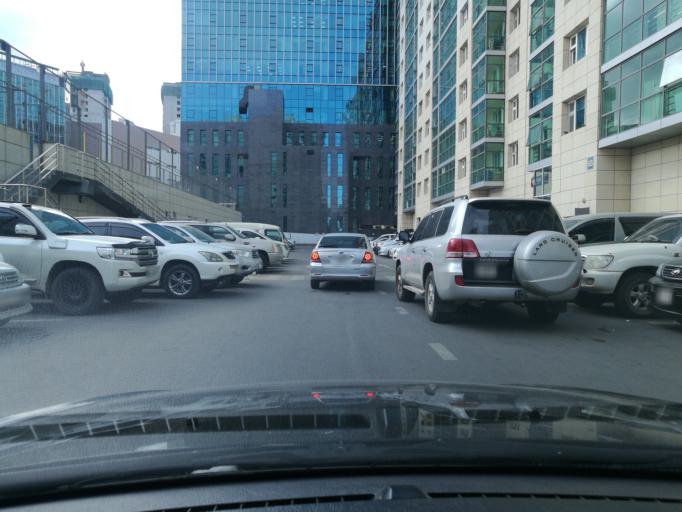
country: MN
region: Ulaanbaatar
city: Ulaanbaatar
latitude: 47.9047
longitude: 106.9129
